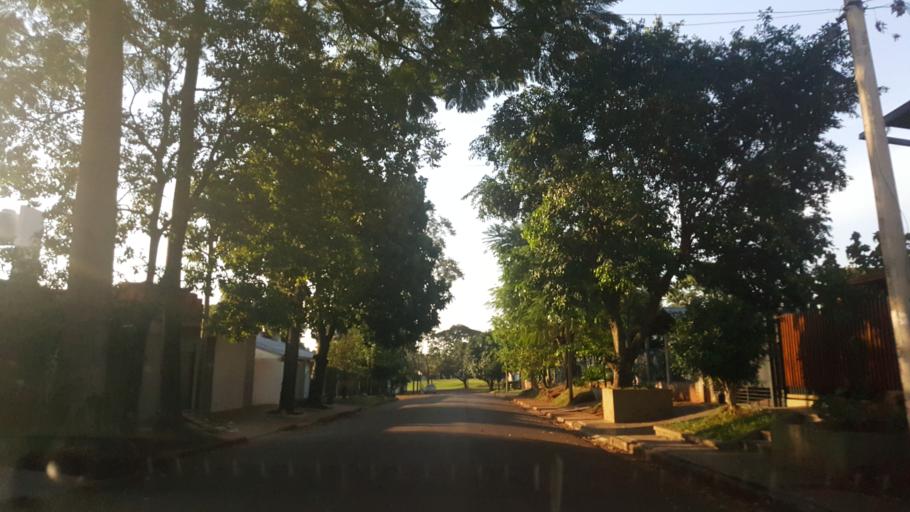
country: AR
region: Misiones
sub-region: Departamento de Capital
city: Posadas
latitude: -27.3906
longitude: -55.9179
